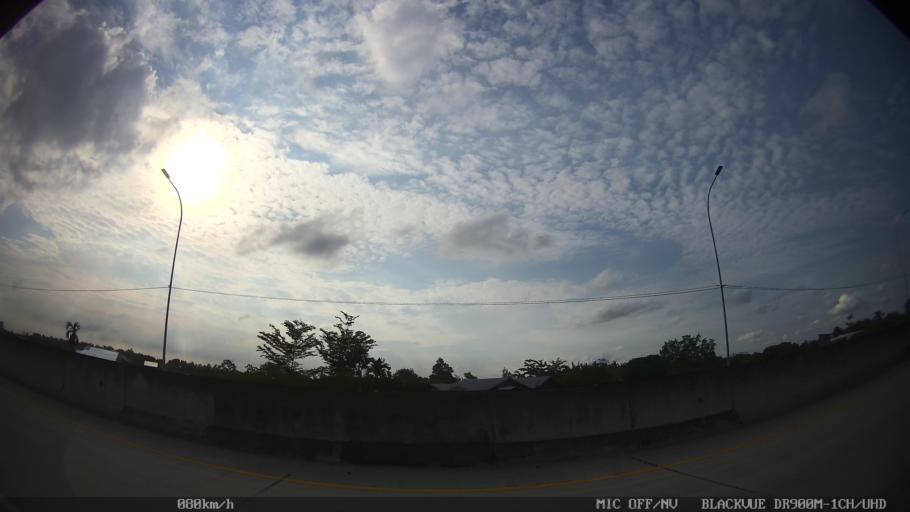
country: ID
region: North Sumatra
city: Medan
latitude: 3.6432
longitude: 98.6478
